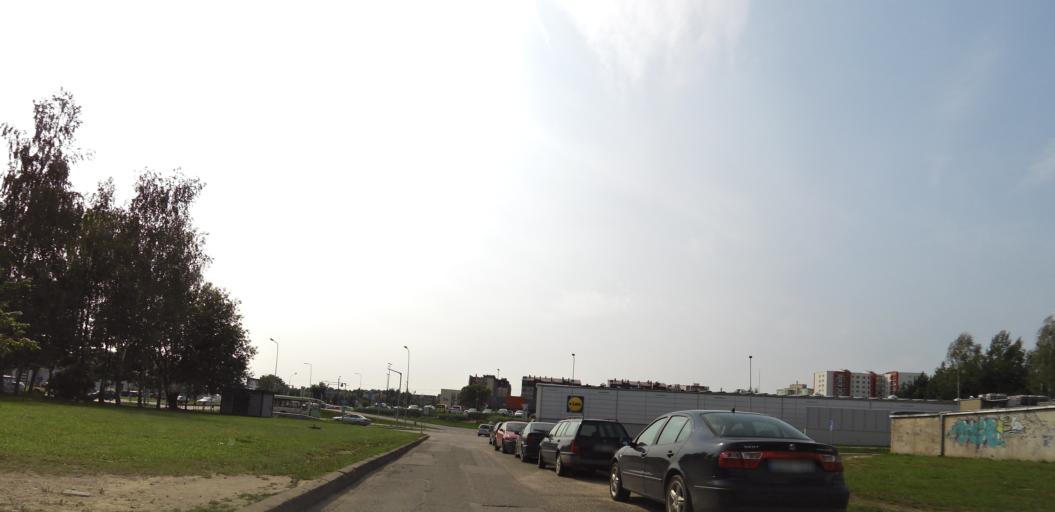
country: LT
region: Vilnius County
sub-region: Vilnius
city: Fabijoniskes
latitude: 54.7384
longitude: 25.2326
